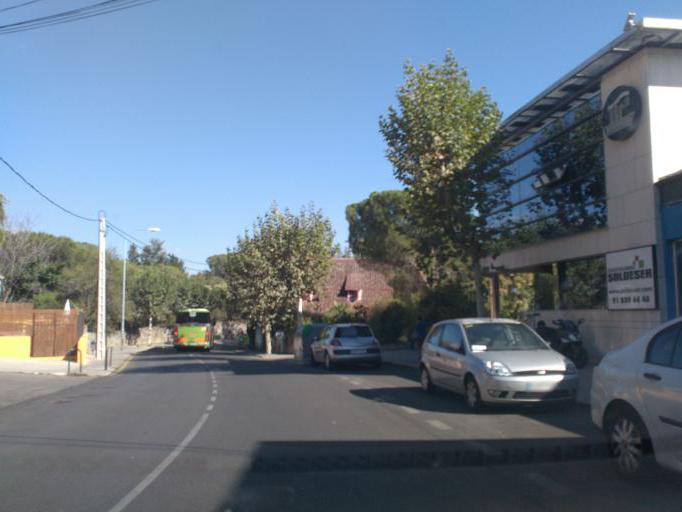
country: ES
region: Madrid
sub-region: Provincia de Madrid
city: Torrelodones
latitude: 40.5766
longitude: -3.9579
